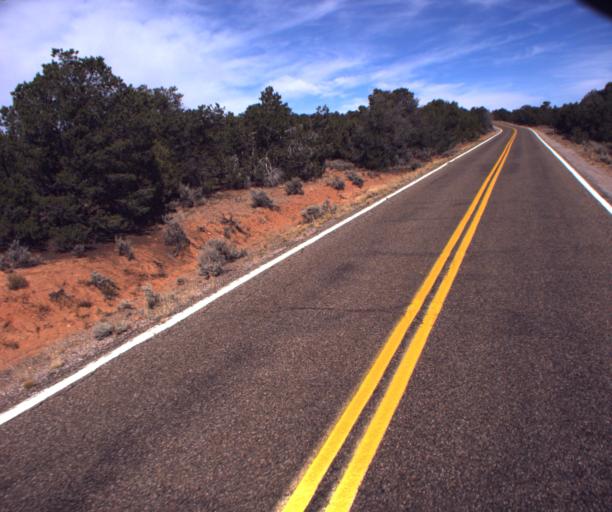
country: US
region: Arizona
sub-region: Navajo County
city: Kayenta
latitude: 36.6280
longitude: -110.5092
